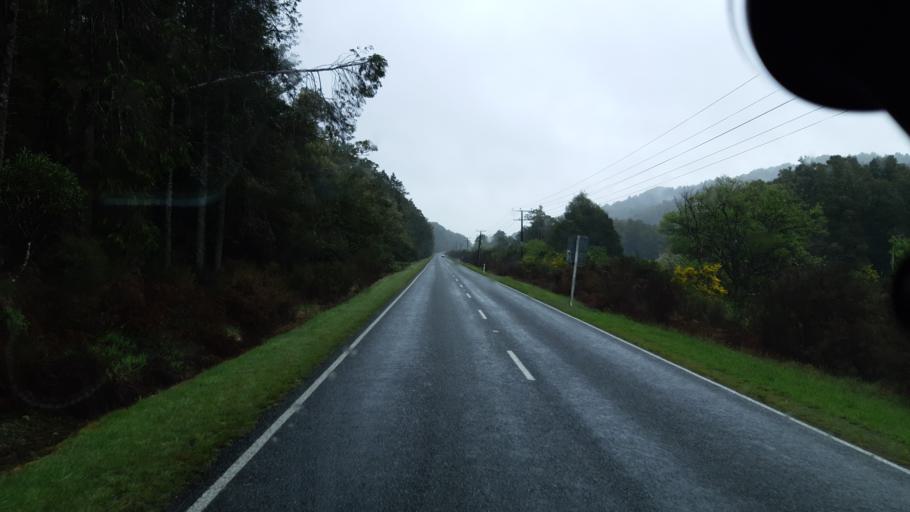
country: NZ
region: West Coast
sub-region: Buller District
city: Westport
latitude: -42.1461
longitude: 171.8121
